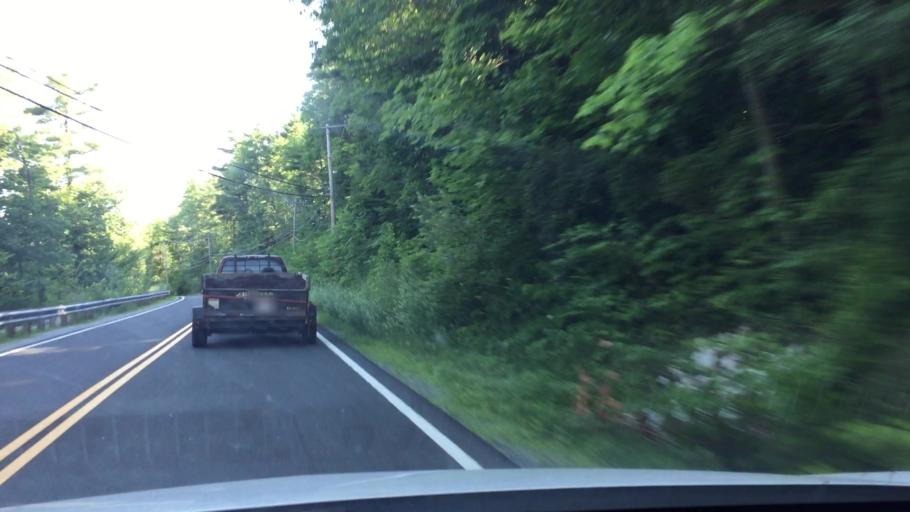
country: US
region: Massachusetts
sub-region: Berkshire County
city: Lee
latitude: 42.2874
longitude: -73.2385
